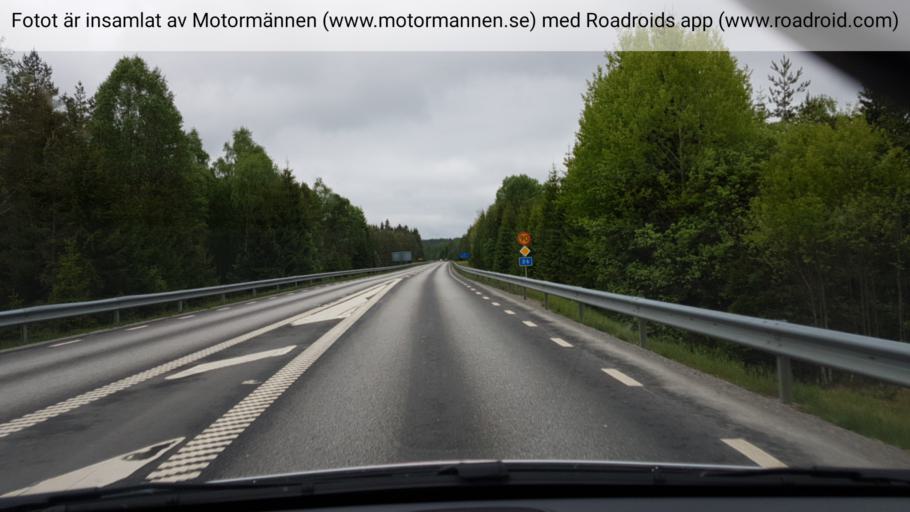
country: SE
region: Joenkoeping
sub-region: Gnosjo Kommun
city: Gnosjoe
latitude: 57.5965
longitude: 13.7390
